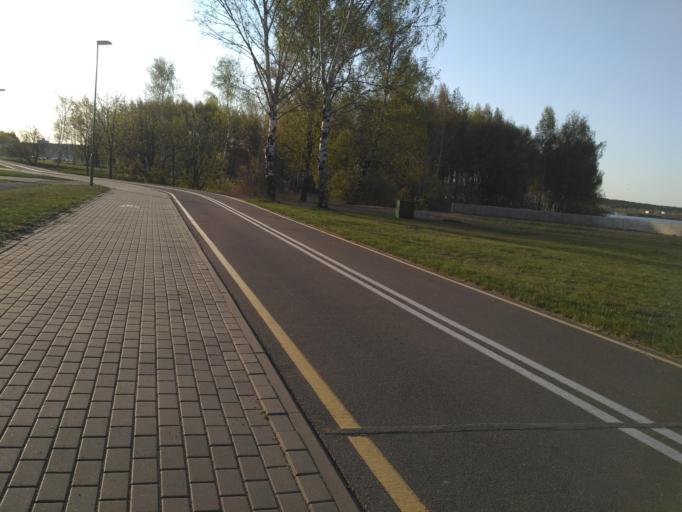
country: BY
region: Minsk
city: Zhdanovichy
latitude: 53.9461
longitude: 27.4590
